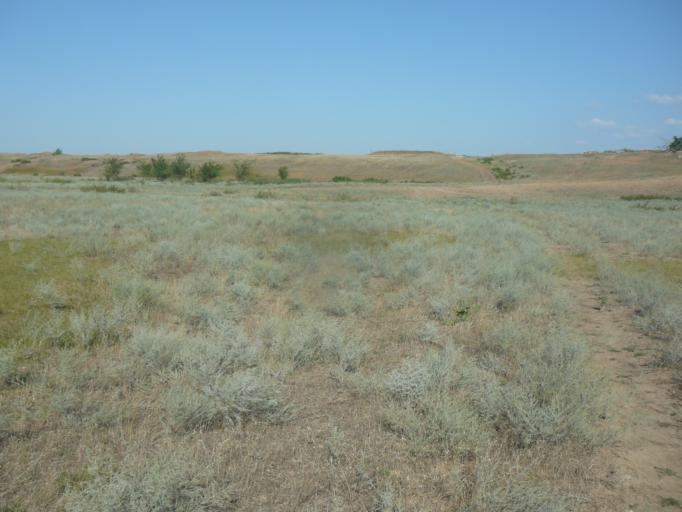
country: RU
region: Saratov
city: Krasnyy Yar
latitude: 51.5672
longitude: 46.5245
